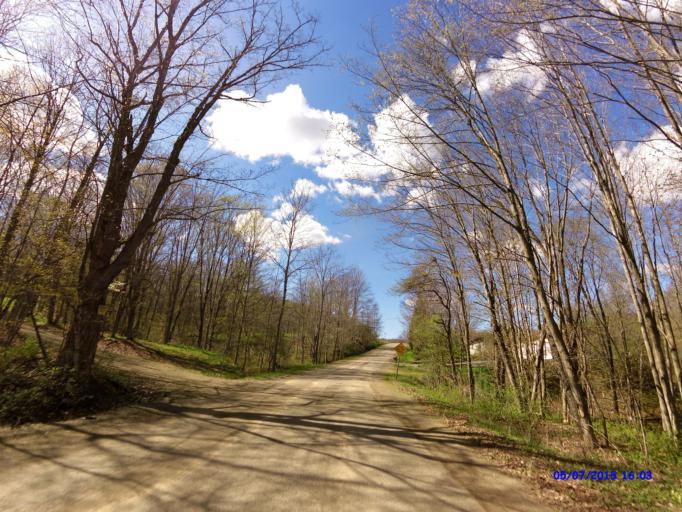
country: US
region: New York
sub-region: Cattaraugus County
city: Franklinville
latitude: 42.2897
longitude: -78.6132
